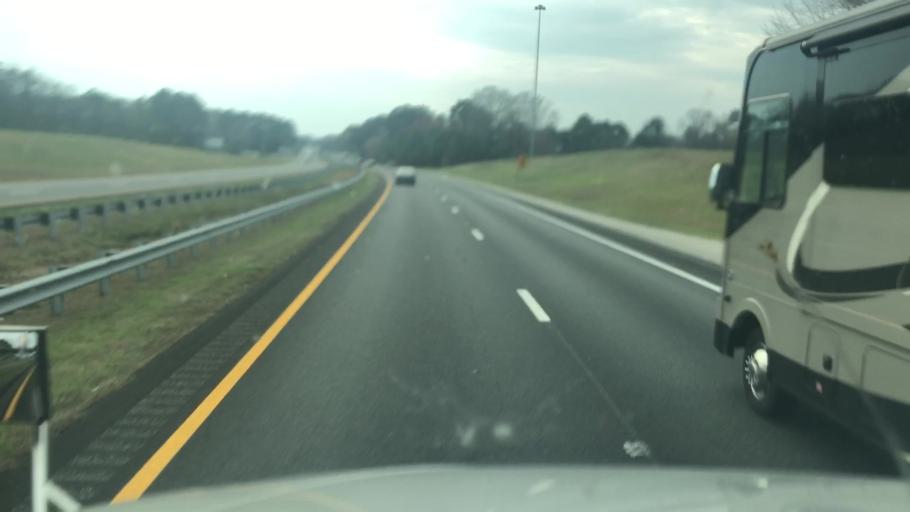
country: US
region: North Carolina
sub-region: Johnston County
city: Four Oaks
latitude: 35.4393
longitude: -78.4210
